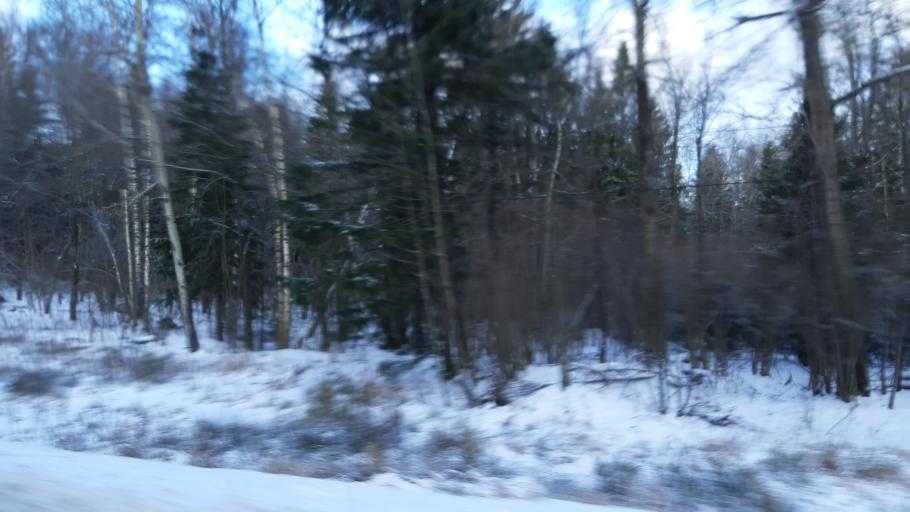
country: RU
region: Moskovskaya
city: Svatkovo
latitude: 56.3164
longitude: 38.3043
